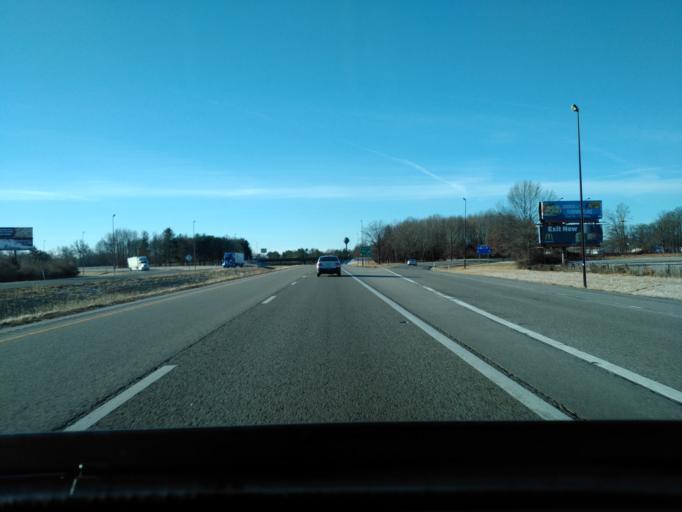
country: US
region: Illinois
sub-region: Franklin County
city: Benton
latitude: 38.0007
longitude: -88.9327
